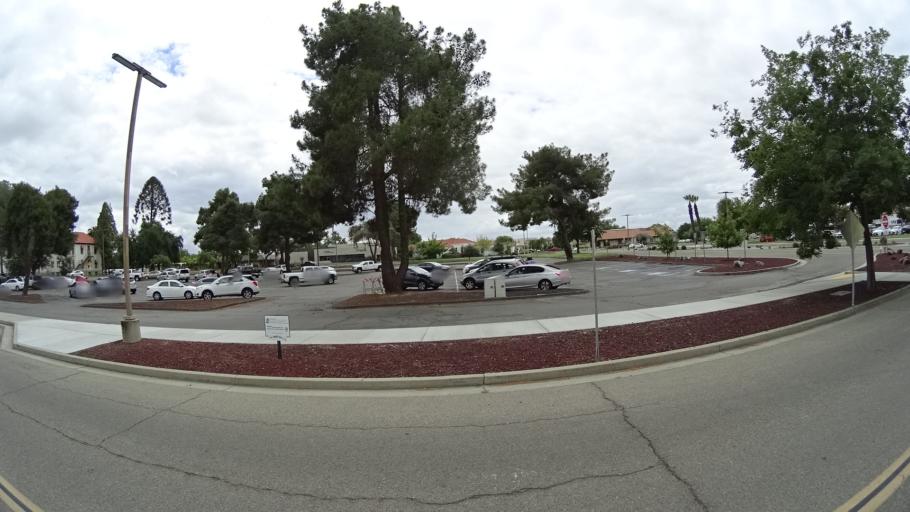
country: US
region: California
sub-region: Kings County
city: Hanford
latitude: 36.3292
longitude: -119.6661
